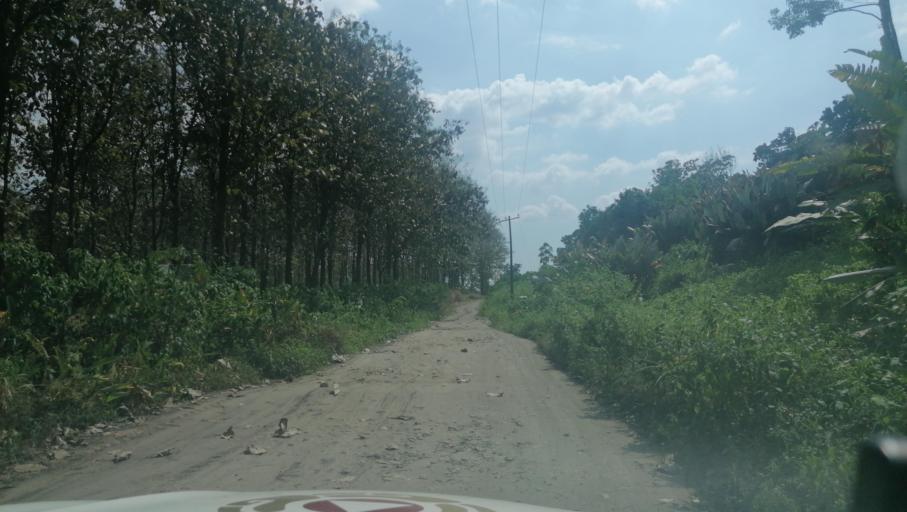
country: MX
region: Chiapas
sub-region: Cacahoatan
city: Benito Juarez
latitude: 15.0267
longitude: -92.2374
